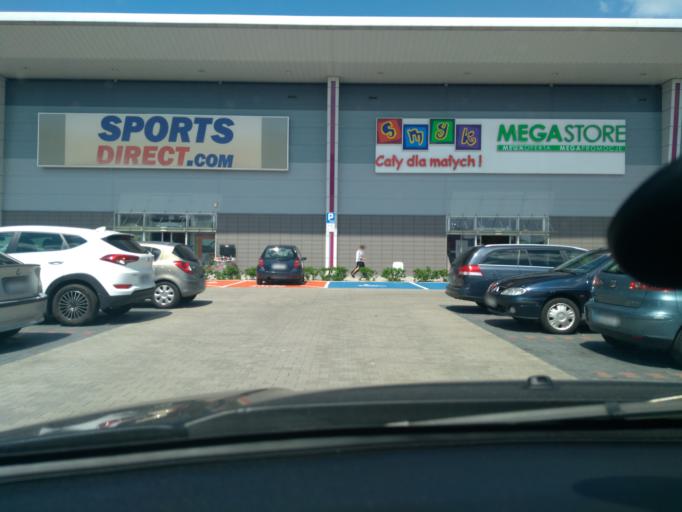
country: PL
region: Silesian Voivodeship
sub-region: Powiat gliwicki
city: Przyszowice
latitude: 50.2670
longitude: 18.7173
